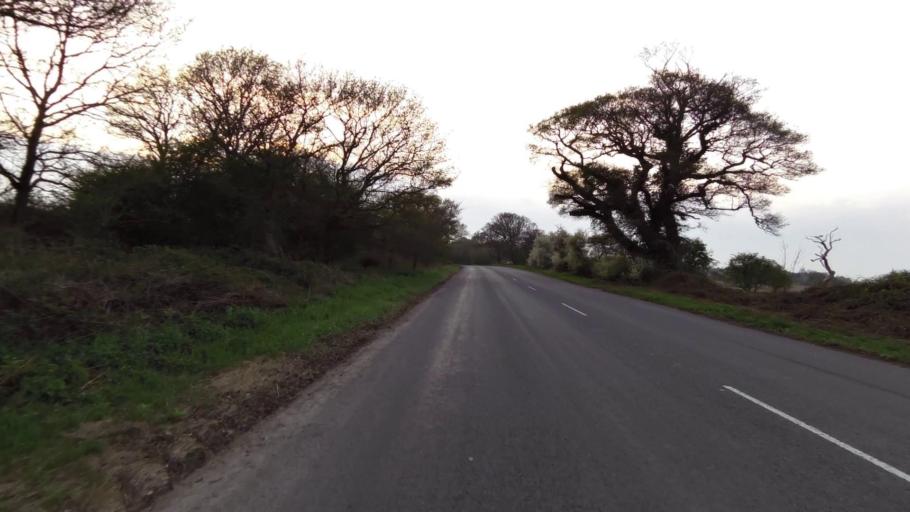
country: GB
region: England
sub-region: Suffolk
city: Kesgrave
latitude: 52.0191
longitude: 1.2600
